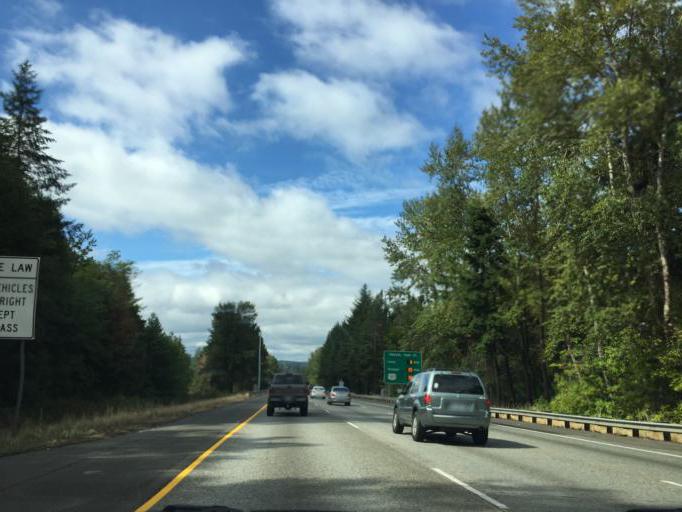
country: US
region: Washington
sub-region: Pierce County
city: DuPont
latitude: 47.0812
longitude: -122.6793
